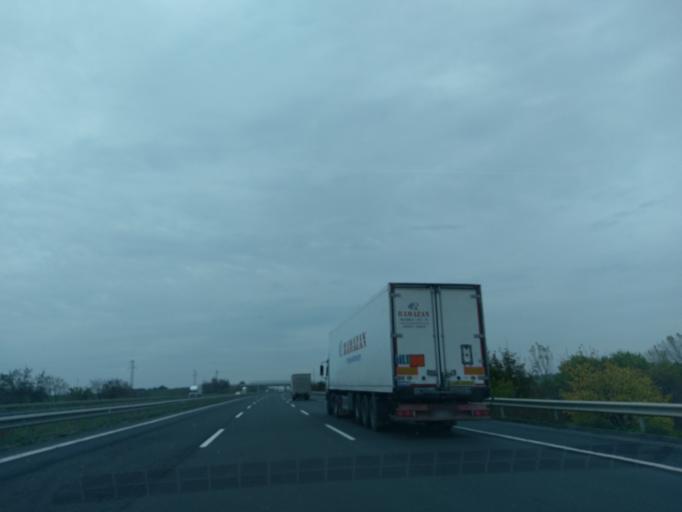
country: TR
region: Istanbul
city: Canta
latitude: 41.1368
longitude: 28.1523
